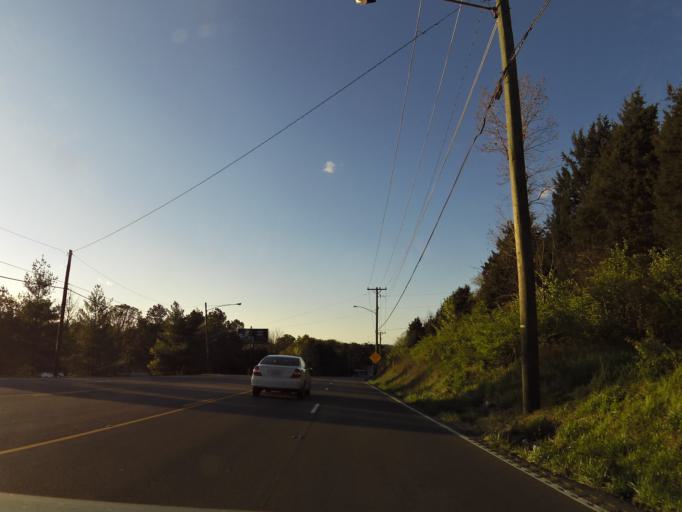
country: US
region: Tennessee
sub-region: Davidson County
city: Goodlettsville
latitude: 36.3314
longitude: -86.7161
